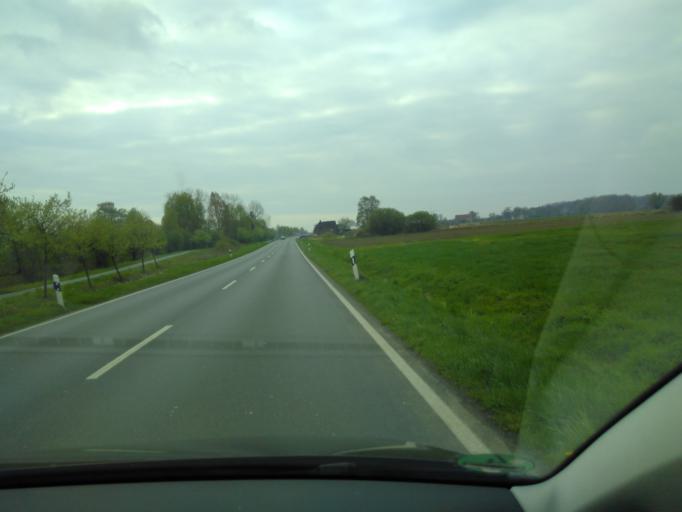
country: DE
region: North Rhine-Westphalia
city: Oelde
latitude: 51.7950
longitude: 8.1383
